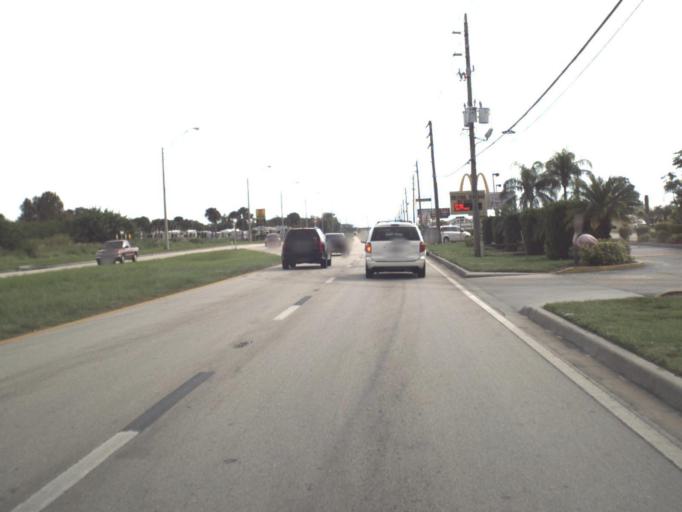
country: US
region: Florida
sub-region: Okeechobee County
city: Okeechobee
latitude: 27.2072
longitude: -80.8299
